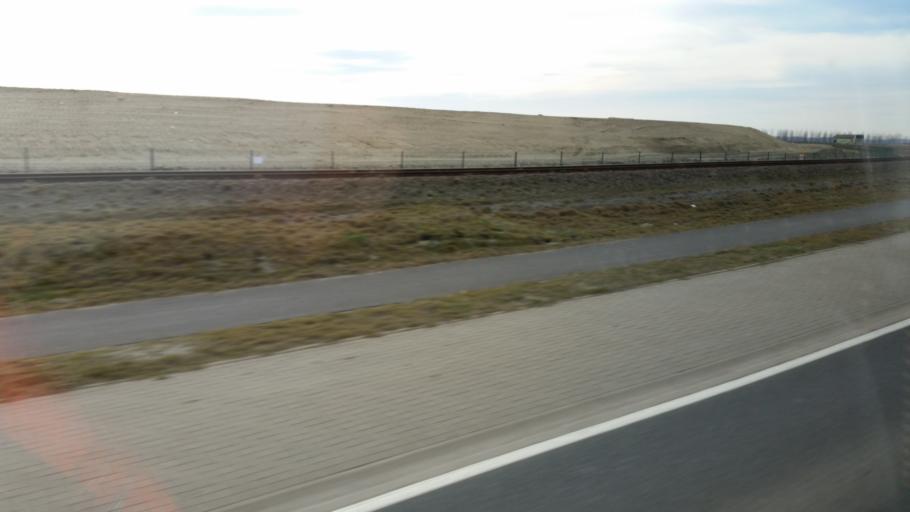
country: BE
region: Flanders
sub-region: Provincie Oost-Vlaanderen
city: Beveren
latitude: 51.3014
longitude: 4.2505
